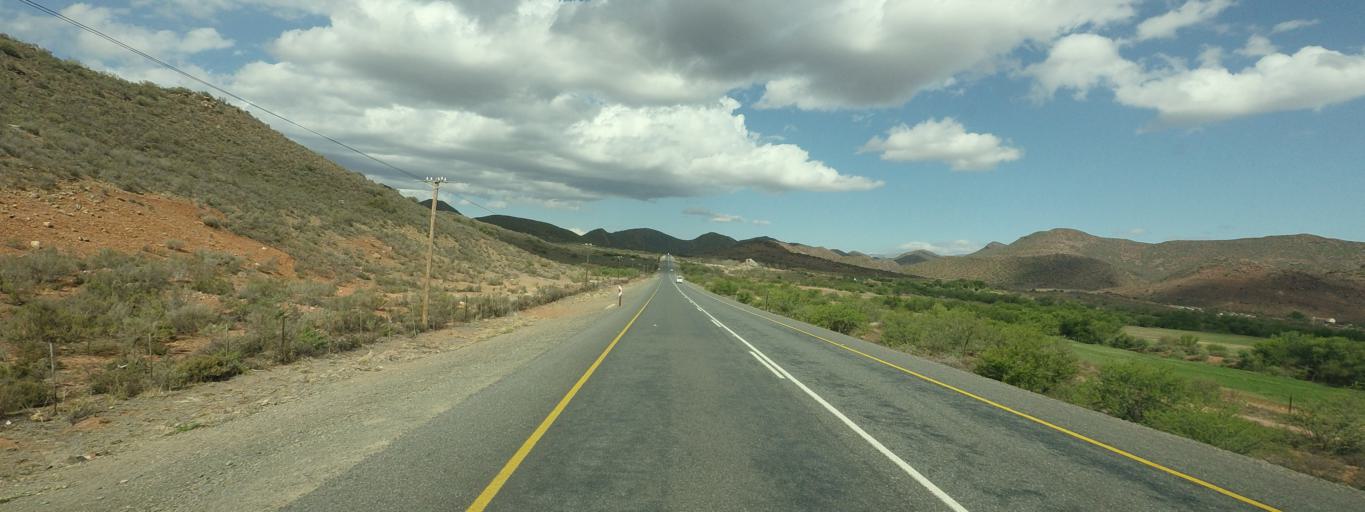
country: ZA
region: Western Cape
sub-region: Eden District Municipality
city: Ladismith
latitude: -33.5060
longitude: 21.2892
